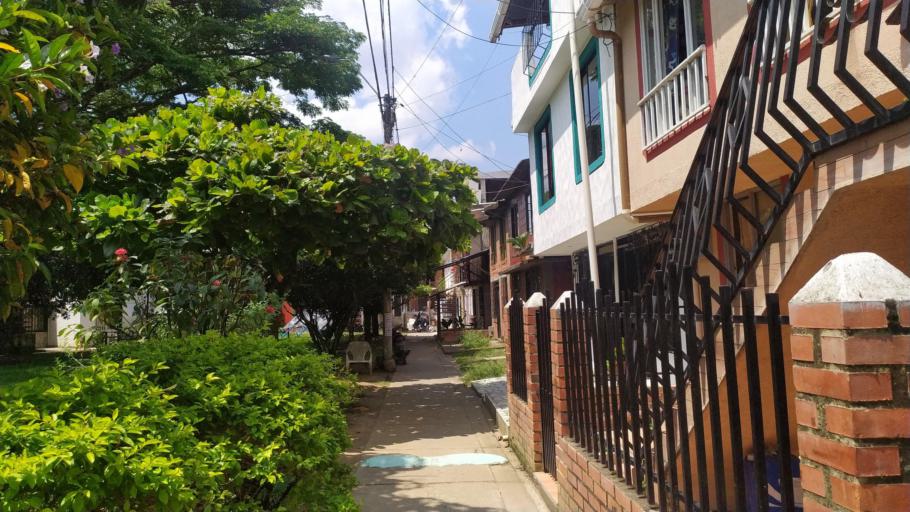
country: CO
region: Valle del Cauca
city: Jamundi
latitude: 3.2507
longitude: -76.5434
